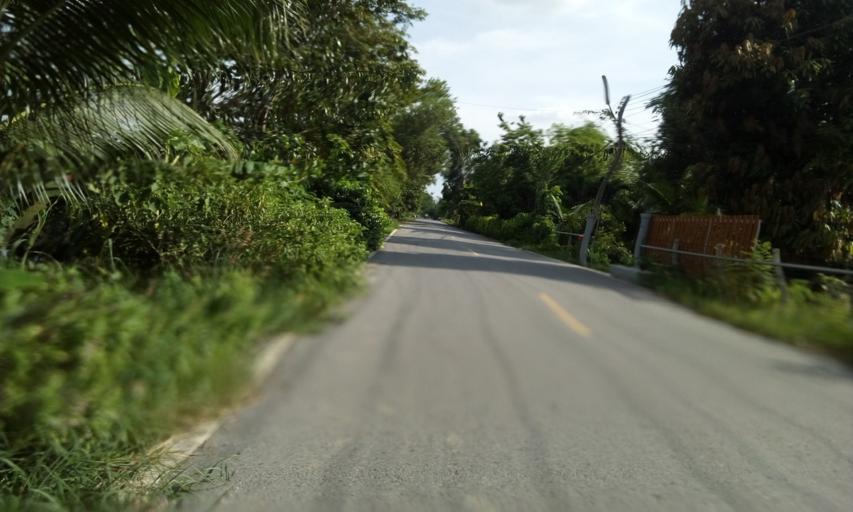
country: TH
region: Pathum Thani
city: Nong Suea
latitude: 14.1731
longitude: 100.8231
